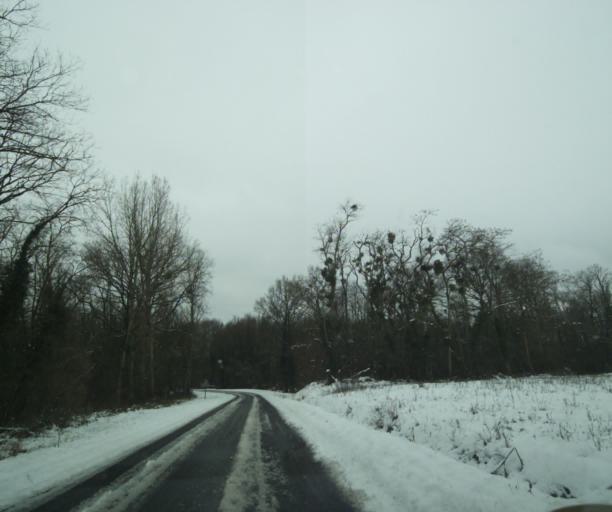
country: FR
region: Champagne-Ardenne
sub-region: Departement de la Haute-Marne
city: Montier-en-Der
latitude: 48.4266
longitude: 4.7280
